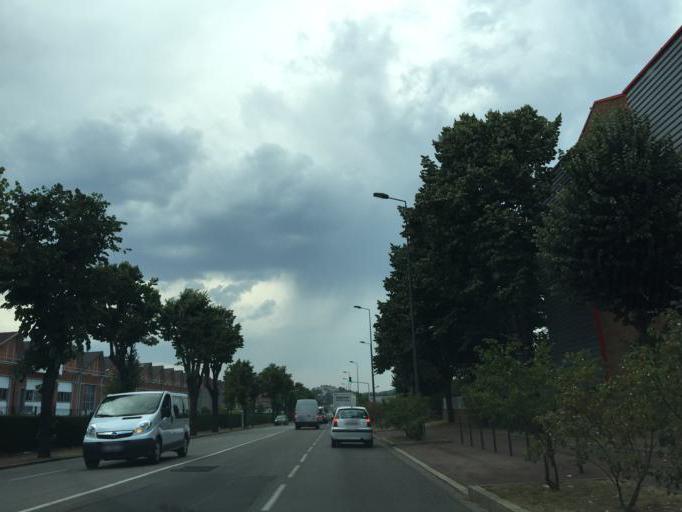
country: FR
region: Rhone-Alpes
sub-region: Departement de la Loire
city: Saint-Etienne
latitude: 45.4545
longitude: 4.3881
